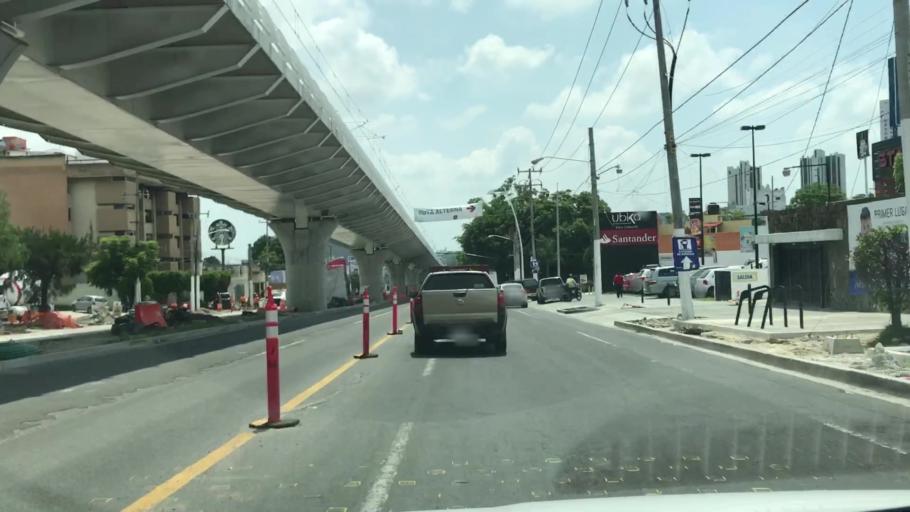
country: MX
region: Jalisco
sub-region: Zapopan
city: Zapopan
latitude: 20.7180
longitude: -103.3841
